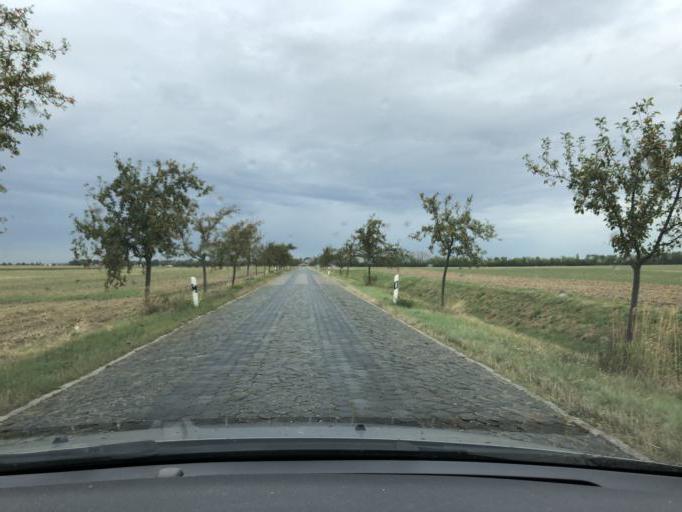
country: DE
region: Saxony-Anhalt
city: Wulfen
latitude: 51.8462
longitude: 11.8724
